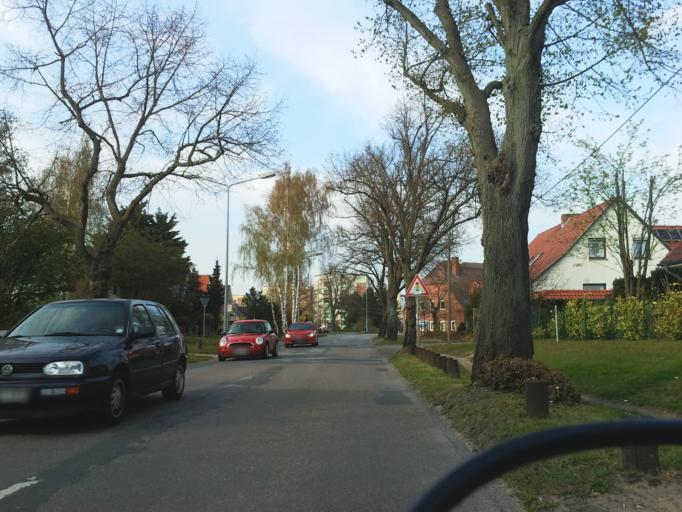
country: DE
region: Mecklenburg-Vorpommern
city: Dierkow-West
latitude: 54.1068
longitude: 12.1555
